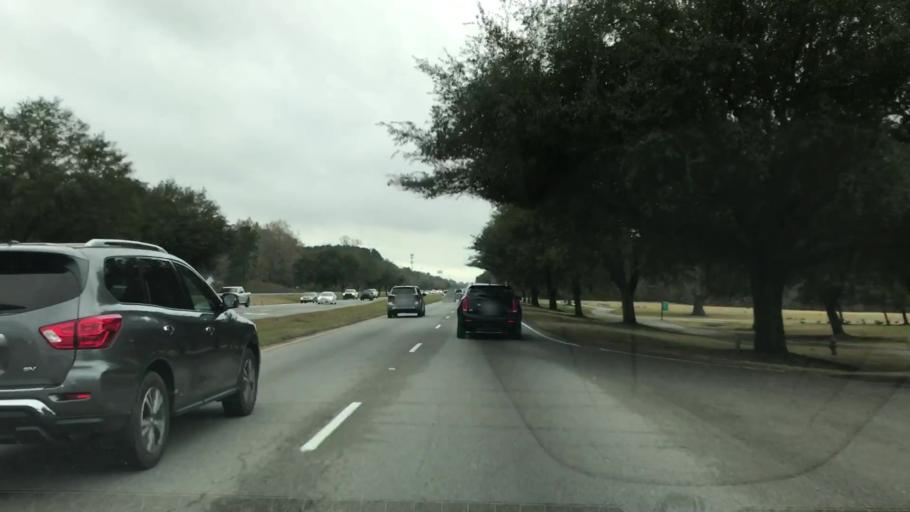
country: US
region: South Carolina
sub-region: Berkeley County
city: Goose Creek
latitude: 33.0278
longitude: -80.0351
